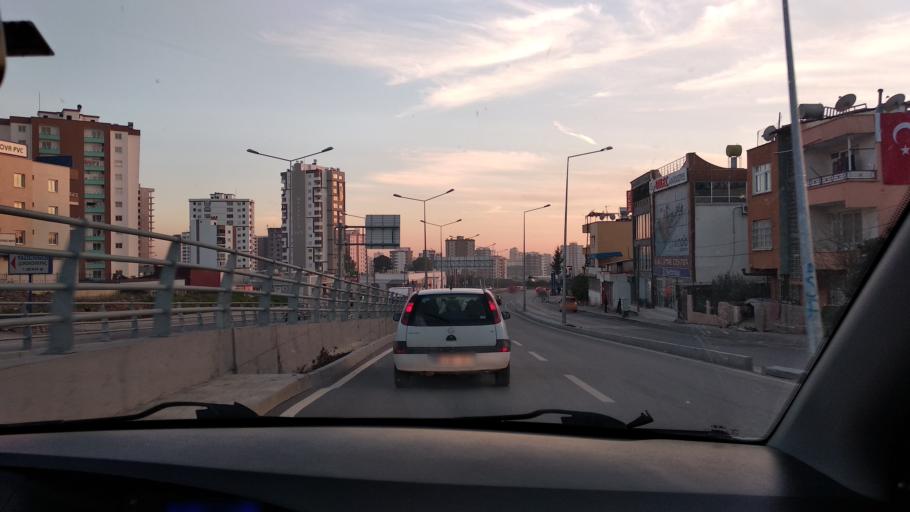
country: TR
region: Mersin
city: Mercin
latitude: 36.8190
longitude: 34.5966
